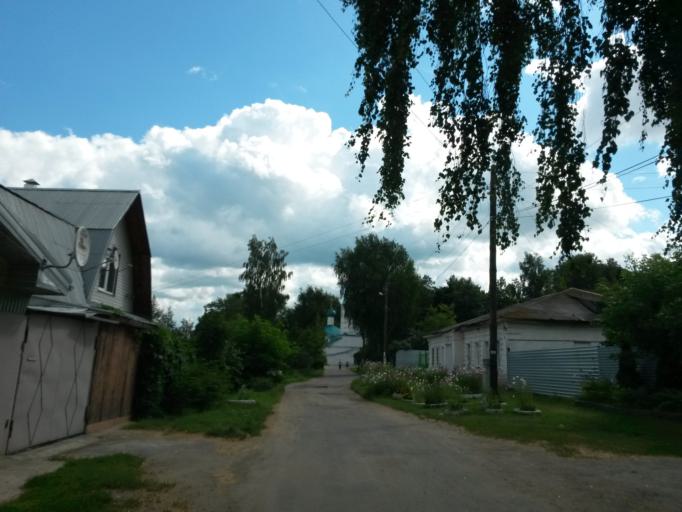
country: RU
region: Jaroslavl
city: Yaroslavl
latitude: 57.6051
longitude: 39.8894
